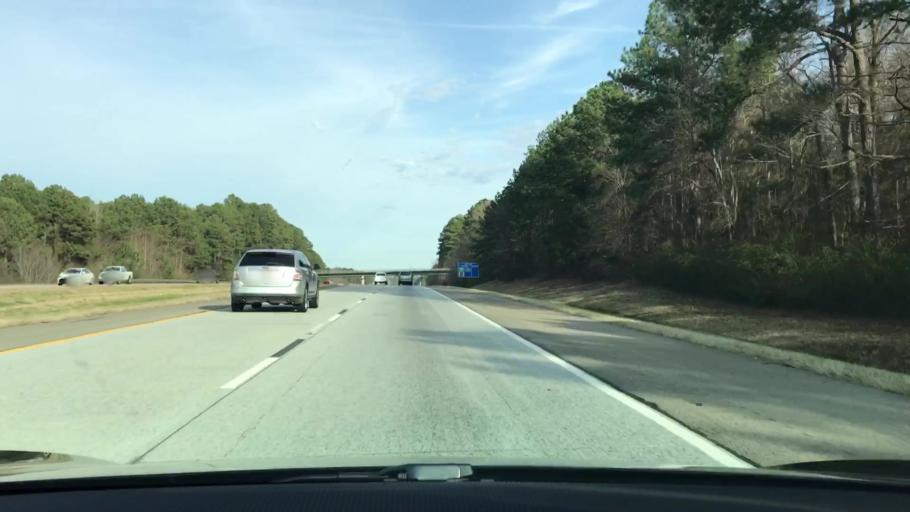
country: US
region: Georgia
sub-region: Greene County
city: Greensboro
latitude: 33.5376
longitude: -83.2388
